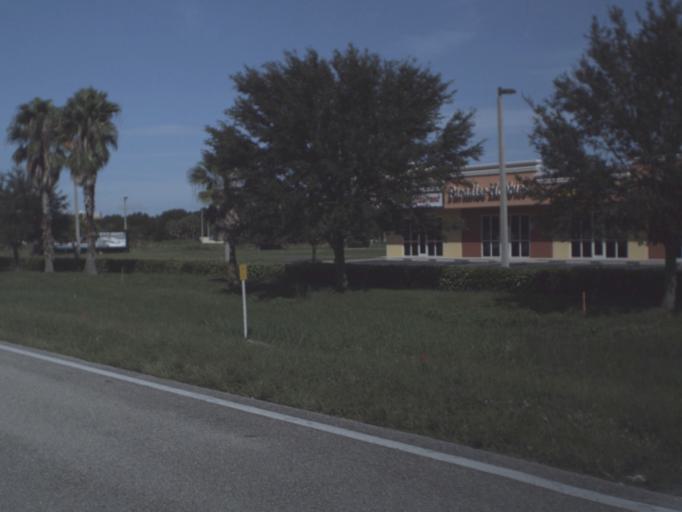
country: US
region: Florida
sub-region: Lee County
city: Fort Myers
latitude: 26.5977
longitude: -81.8425
